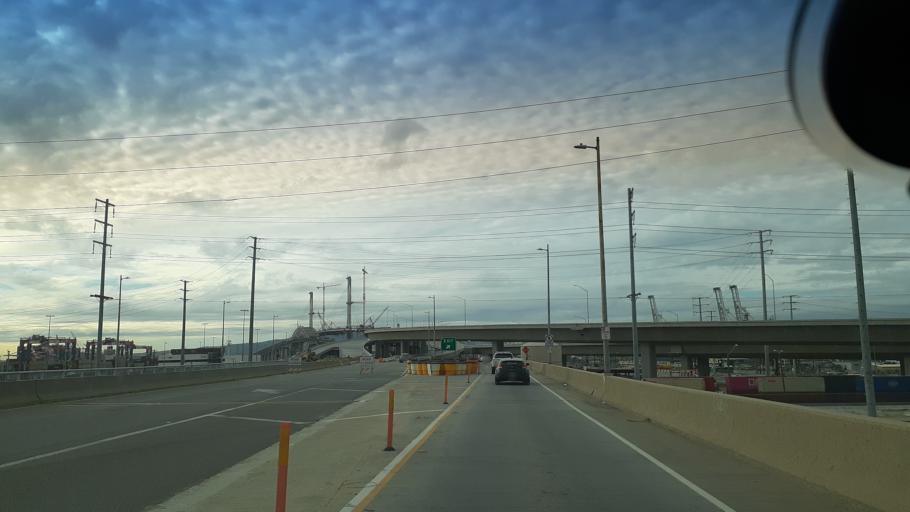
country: US
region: California
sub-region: Los Angeles County
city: Long Beach
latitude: 33.7674
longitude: -118.2060
